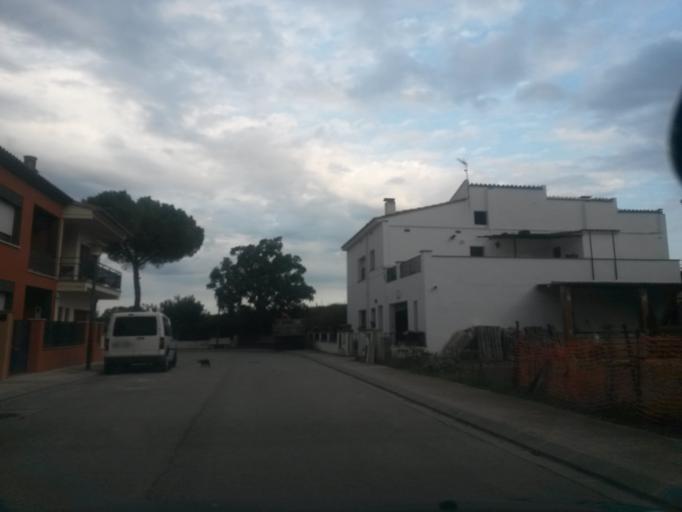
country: ES
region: Catalonia
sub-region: Provincia de Girona
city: Vilablareix
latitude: 41.9694
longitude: 2.7630
